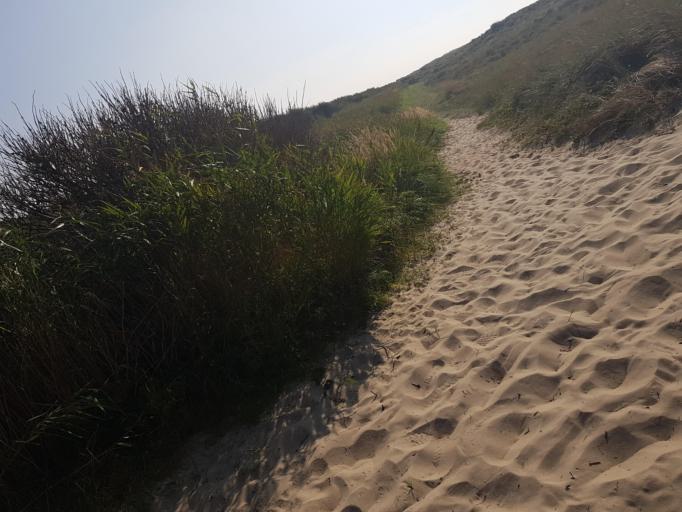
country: NL
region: North Holland
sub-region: Gemeente Texel
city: Den Burg
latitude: 53.1158
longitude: 4.7725
